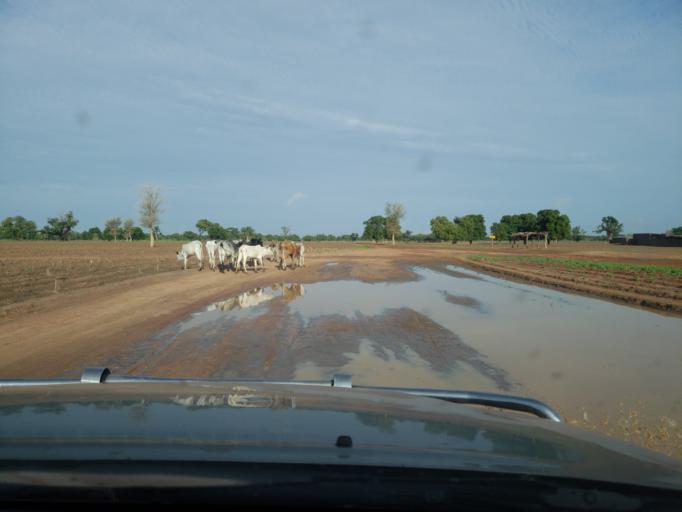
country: ML
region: Sikasso
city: Koutiala
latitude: 12.4215
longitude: -5.6893
